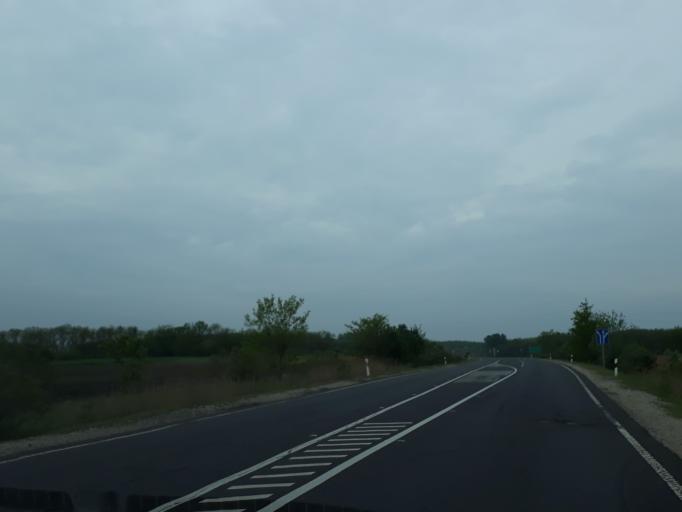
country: HU
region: Szabolcs-Szatmar-Bereg
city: Demecser
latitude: 48.0673
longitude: 21.9370
